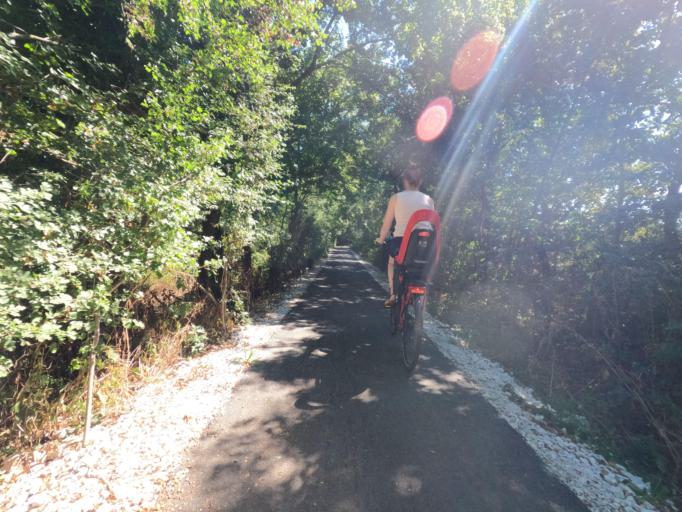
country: DE
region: North Rhine-Westphalia
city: Wegberg
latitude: 51.1318
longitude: 6.3036
